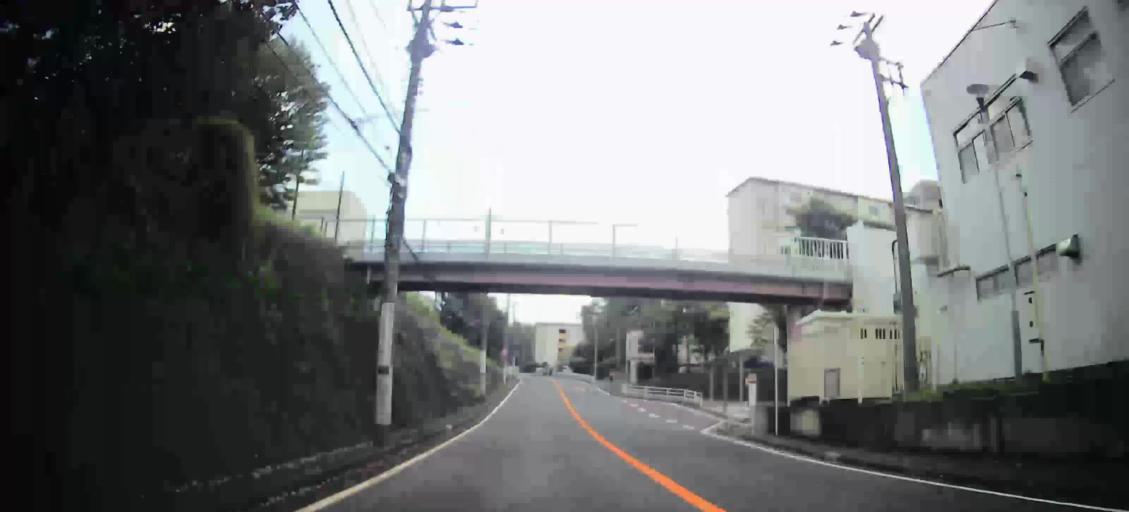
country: JP
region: Kanagawa
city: Yokohama
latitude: 35.4601
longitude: 139.5503
